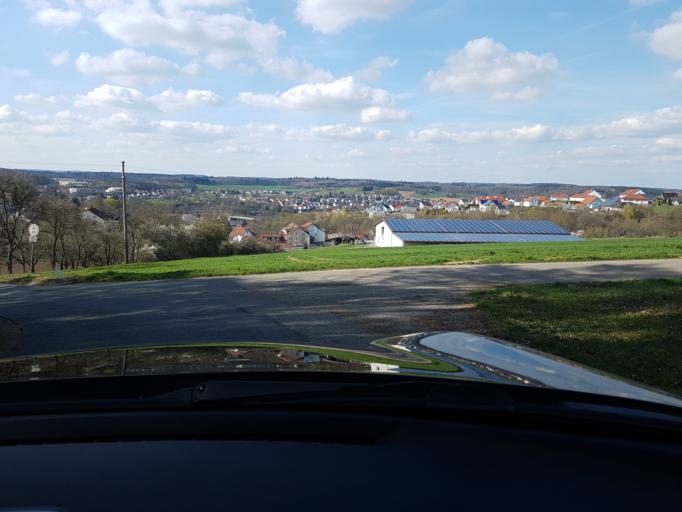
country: DE
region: Baden-Wuerttemberg
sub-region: Karlsruhe Region
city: Osterburken
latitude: 49.4226
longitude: 9.4319
